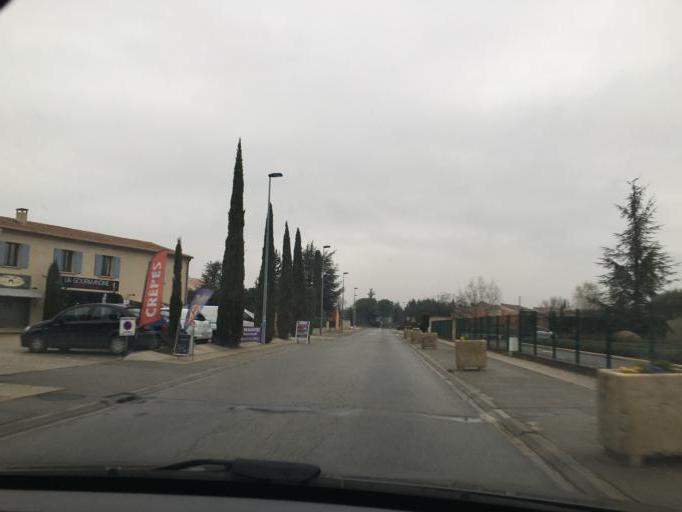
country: FR
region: Provence-Alpes-Cote d'Azur
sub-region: Departement du Vaucluse
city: Maubec
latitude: 43.8700
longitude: 5.1459
